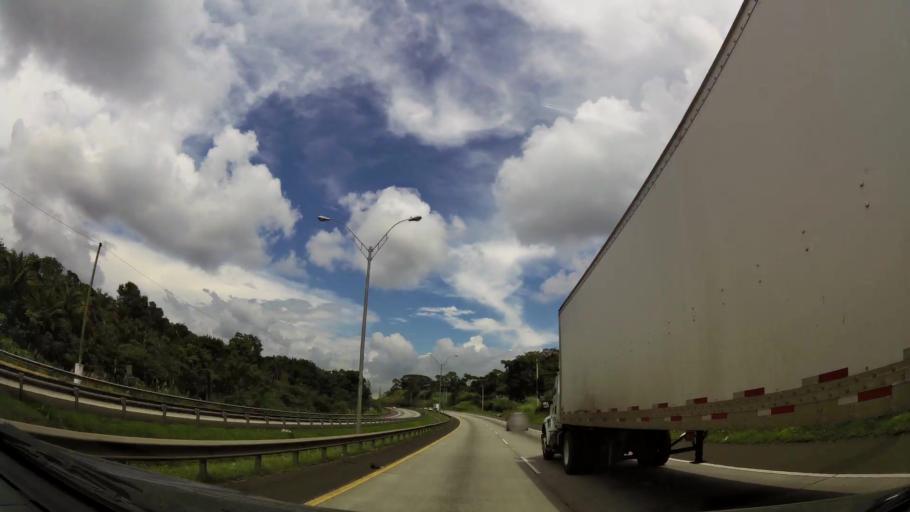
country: PA
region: Panama
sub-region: Distrito de Panama
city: Paraiso
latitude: 9.0018
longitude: -79.6504
